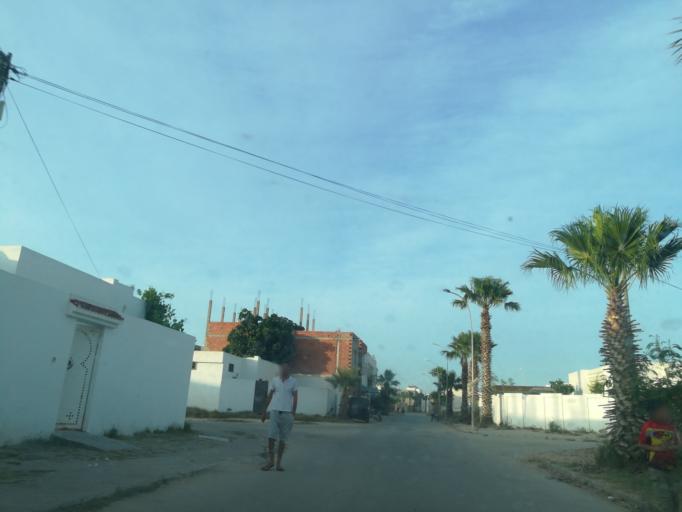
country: TN
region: Safaqis
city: Al Qarmadah
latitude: 34.8243
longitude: 10.7560
